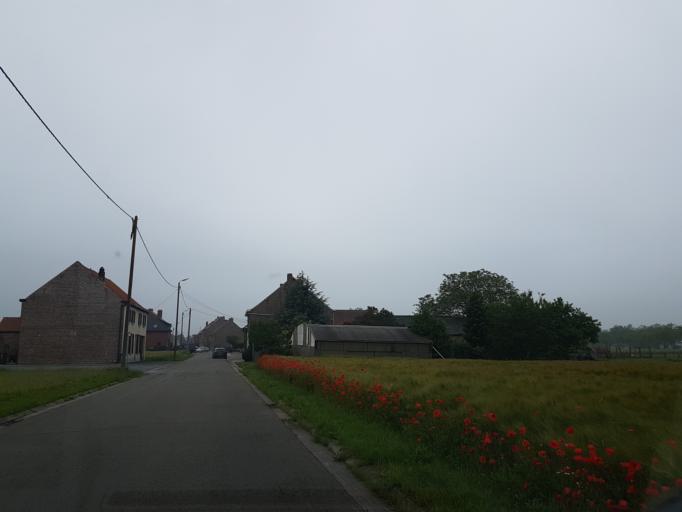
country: BE
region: Flanders
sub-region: Provincie Vlaams-Brabant
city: Steenokkerzeel
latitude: 50.9330
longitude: 4.4817
